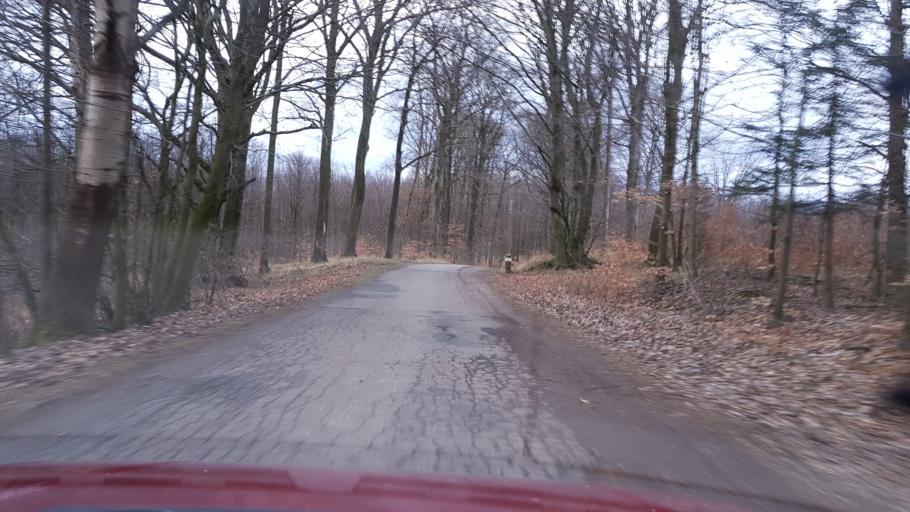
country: PL
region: West Pomeranian Voivodeship
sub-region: Powiat gryfinski
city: Stare Czarnowo
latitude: 53.3245
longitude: 14.6982
